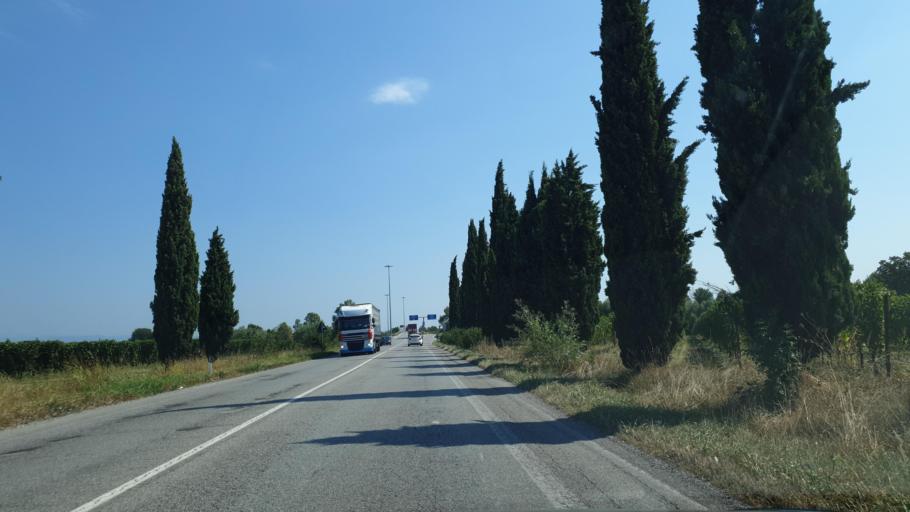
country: IT
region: Lombardy
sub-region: Provincia di Brescia
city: San Martino della Battaglia
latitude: 45.4453
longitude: 10.5893
